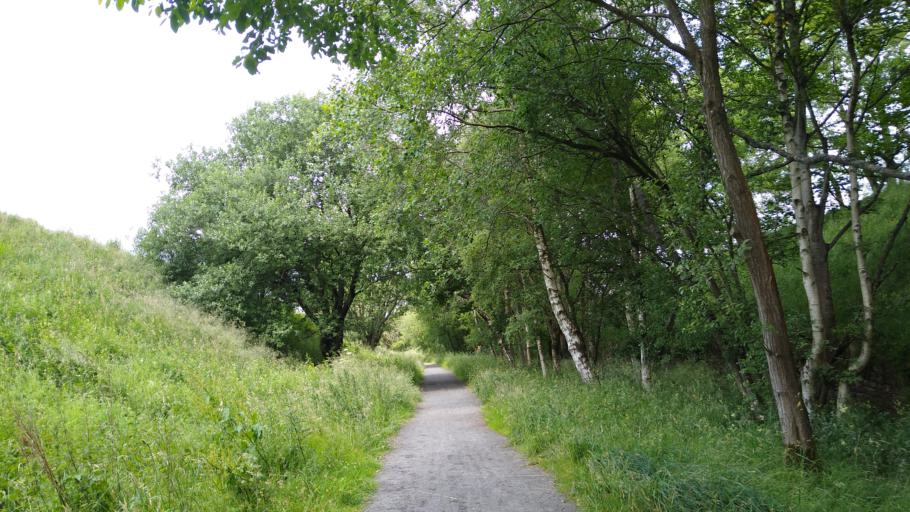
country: GB
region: England
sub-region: Northumberland
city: Greenhead
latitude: 54.9311
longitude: -2.5015
